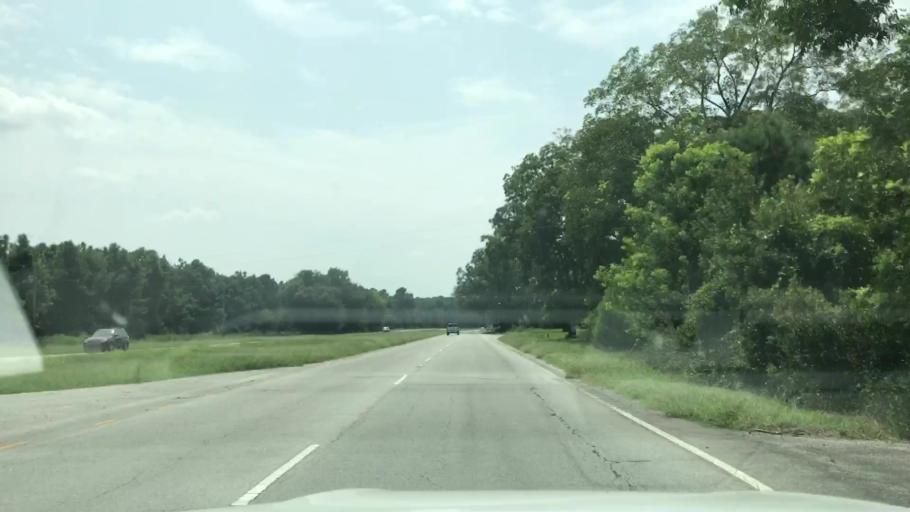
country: US
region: South Carolina
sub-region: Charleston County
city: Awendaw
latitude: 33.0575
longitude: -79.5436
